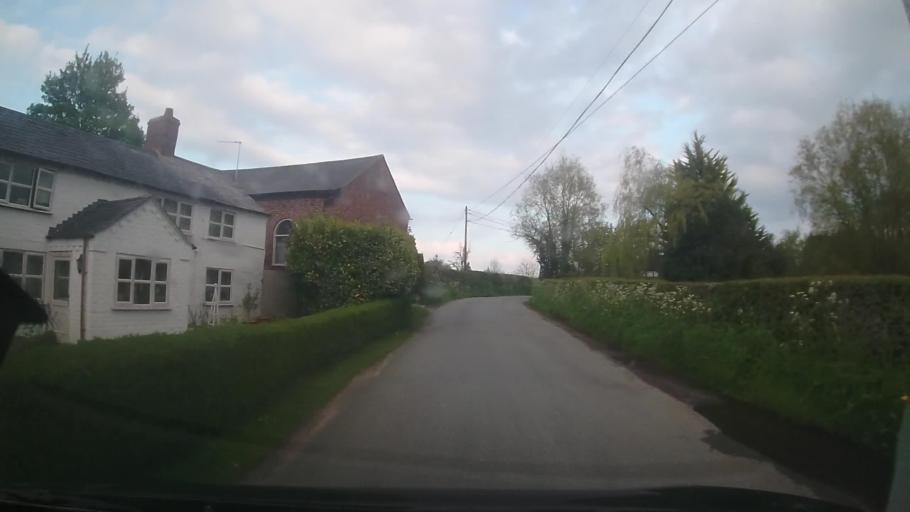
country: GB
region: England
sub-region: Shropshire
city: Ellesmere
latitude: 52.9219
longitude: -2.8241
